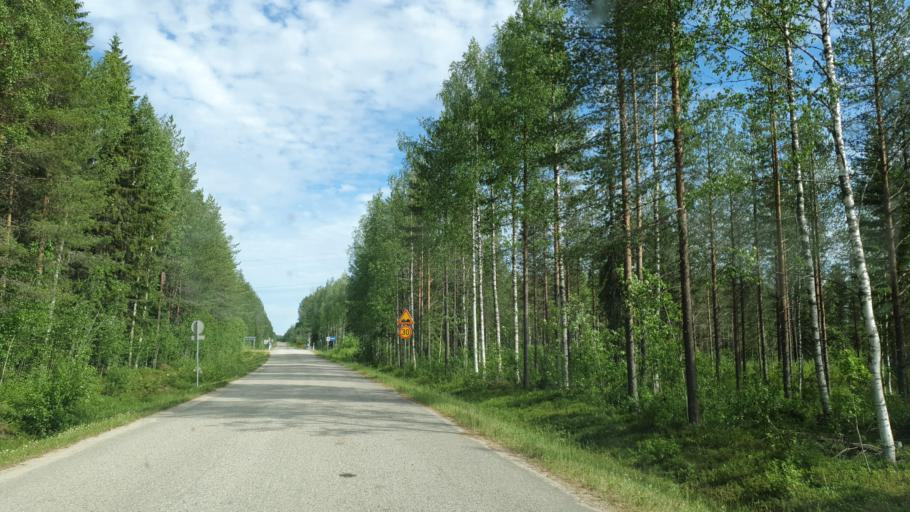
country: FI
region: Kainuu
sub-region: Kehys-Kainuu
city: Kuhmo
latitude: 64.5159
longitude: 29.3966
